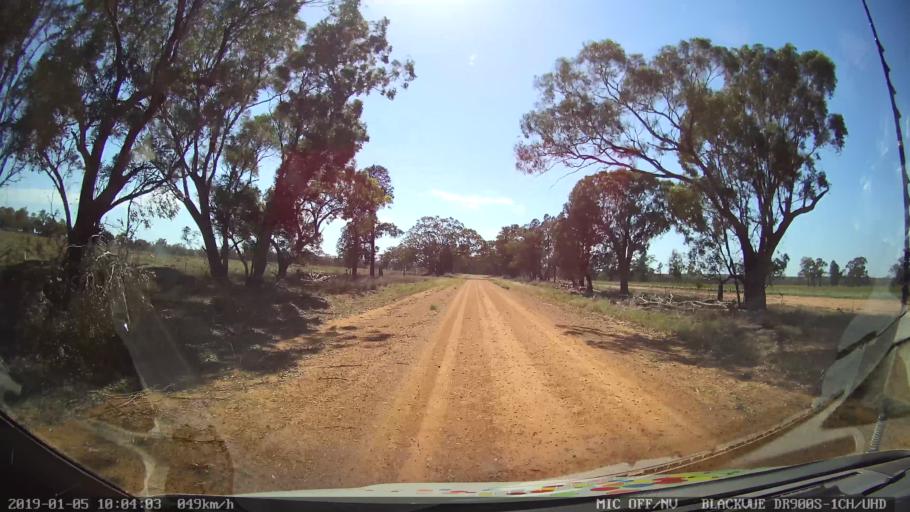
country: AU
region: New South Wales
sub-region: Gilgandra
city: Gilgandra
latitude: -31.6726
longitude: 148.8575
